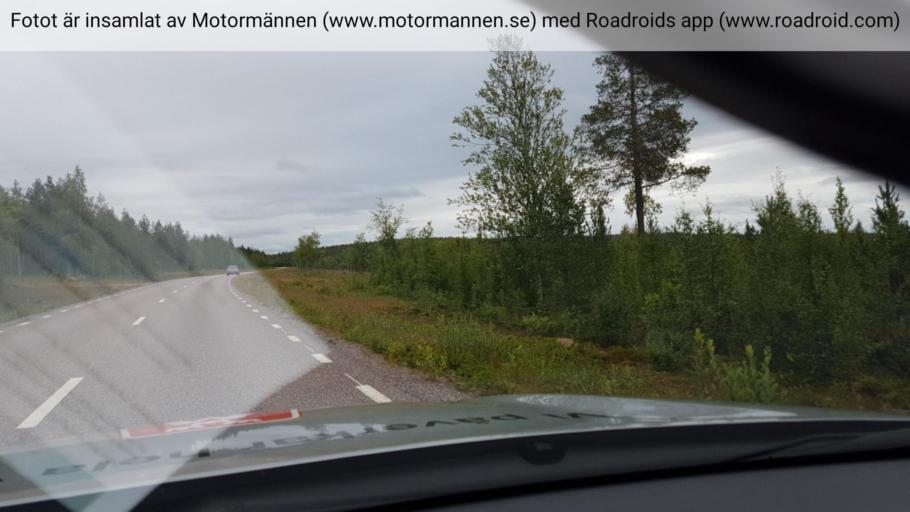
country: SE
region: Norrbotten
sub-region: Gallivare Kommun
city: Gaellivare
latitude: 67.0437
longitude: 21.6371
